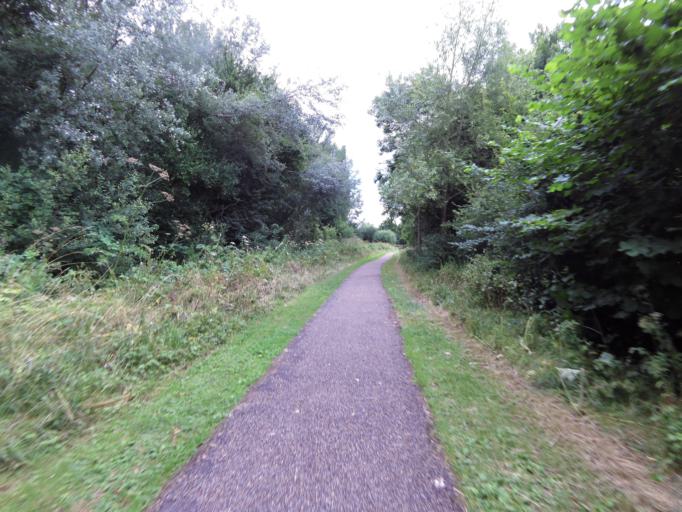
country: GB
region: England
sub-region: Essex
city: Waltham Abbey
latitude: 51.6964
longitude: -0.0173
